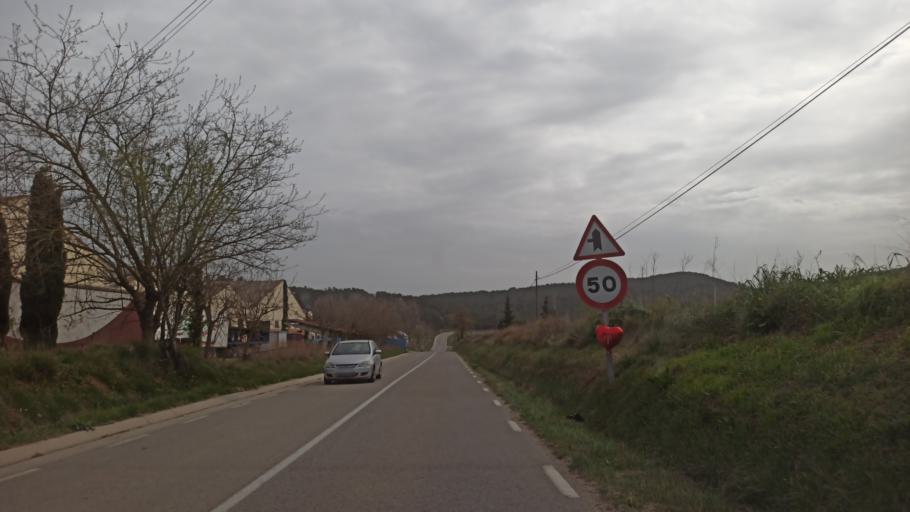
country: ES
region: Catalonia
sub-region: Provincia de Barcelona
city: Avinyonet del Penedes
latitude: 41.3397
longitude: 1.7461
